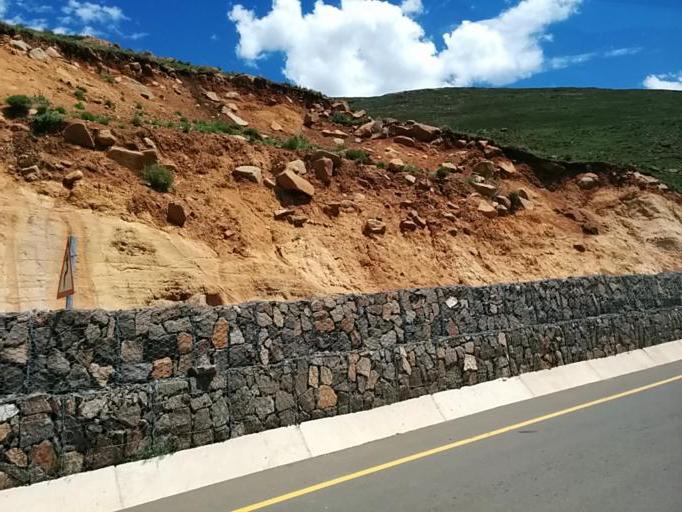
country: LS
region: Maseru
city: Nako
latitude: -29.9203
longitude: 28.1508
